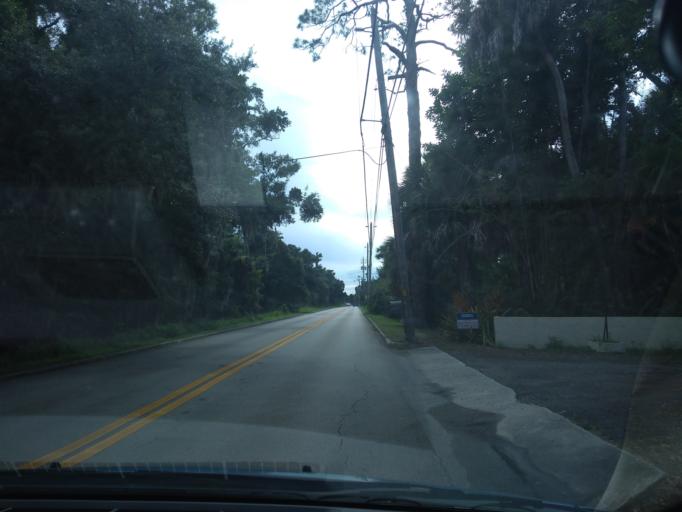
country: US
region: Florida
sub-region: Indian River County
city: Vero Beach South
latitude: 27.6314
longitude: -80.4351
